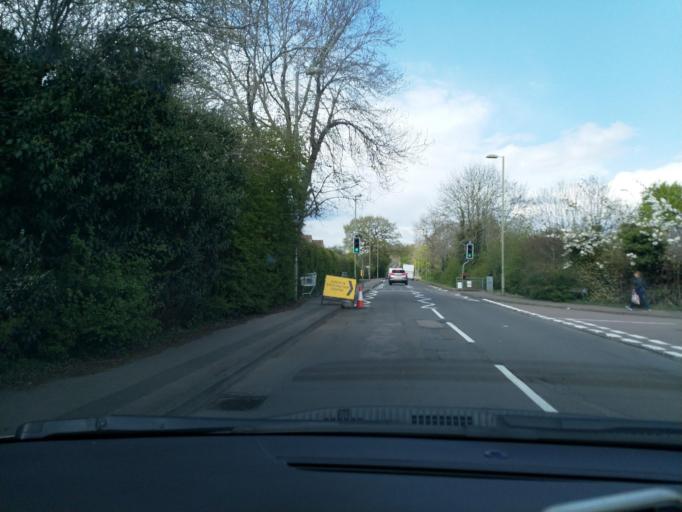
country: GB
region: England
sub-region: Suffolk
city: Woodbridge
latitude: 52.0671
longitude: 1.3211
